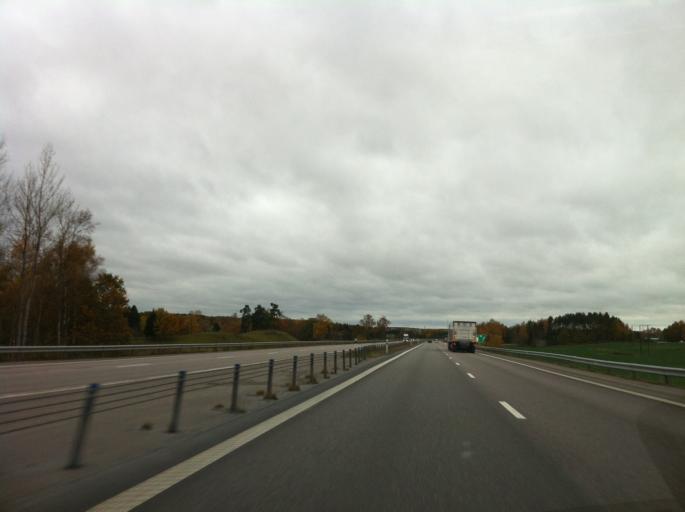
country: SE
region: OEstergoetland
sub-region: Mjolby Kommun
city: Mjolby
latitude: 58.3475
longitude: 15.1890
